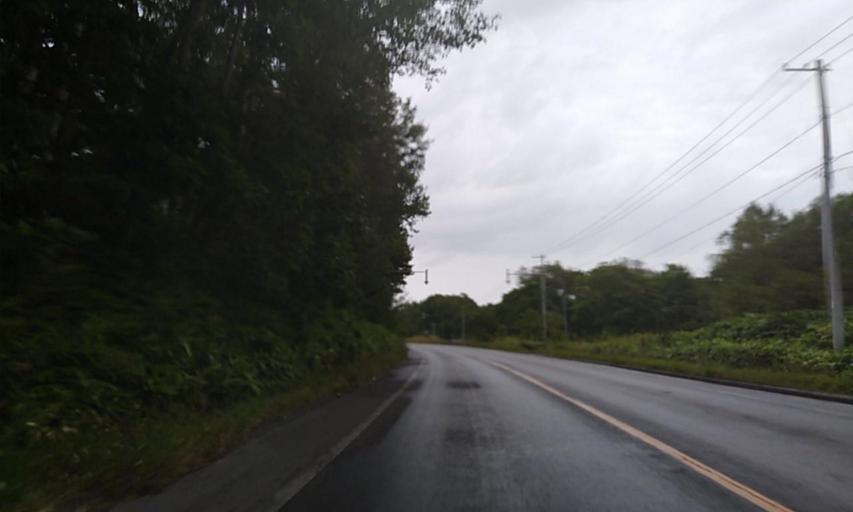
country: JP
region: Hokkaido
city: Mombetsu
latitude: 44.4882
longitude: 143.0877
